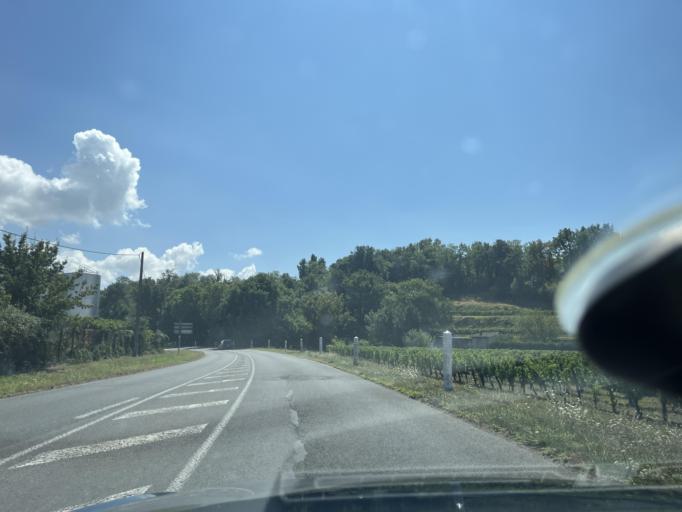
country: FR
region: Aquitaine
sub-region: Departement de la Gironde
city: Cars
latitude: 45.0793
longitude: -0.6356
